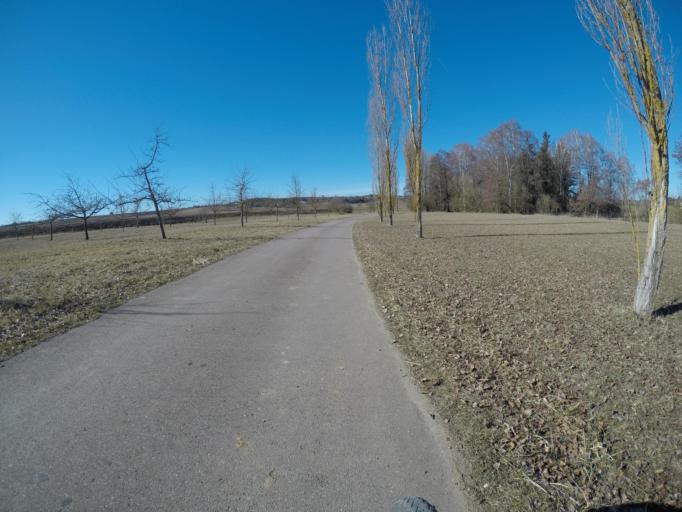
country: DE
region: Baden-Wuerttemberg
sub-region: Regierungsbezirk Stuttgart
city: Herrenberg
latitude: 48.5708
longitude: 8.8747
